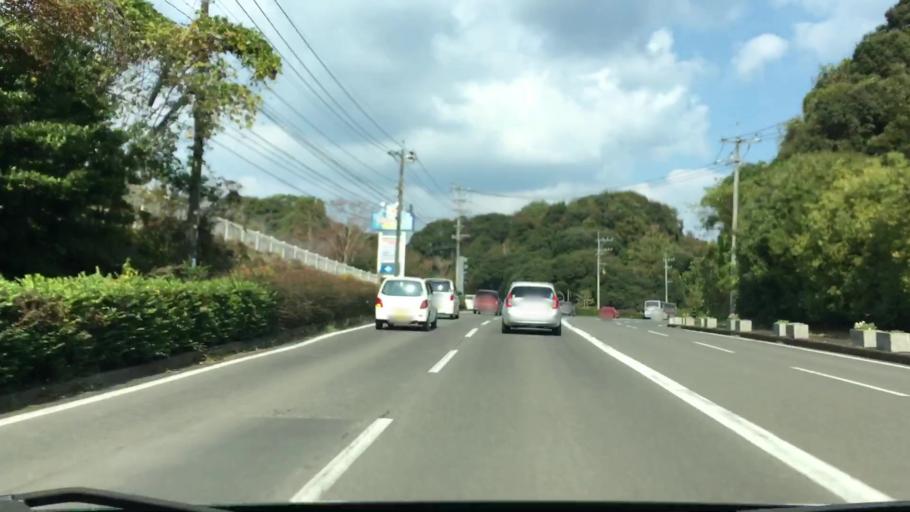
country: JP
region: Nagasaki
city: Sasebo
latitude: 32.9900
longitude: 129.7491
